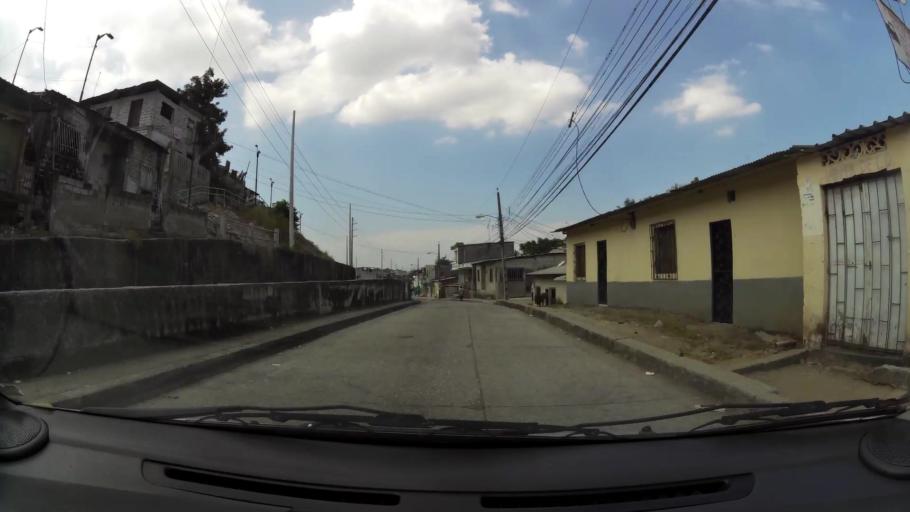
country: EC
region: Guayas
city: Santa Lucia
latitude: -2.1337
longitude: -79.9445
